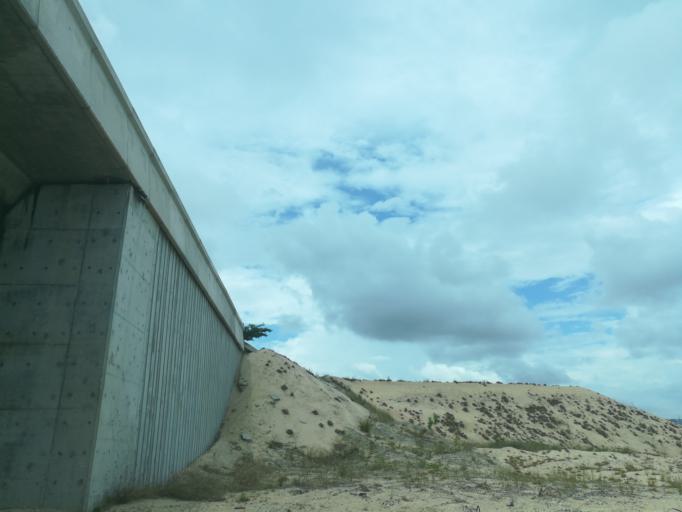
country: NG
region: Lagos
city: Ikoyi
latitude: 6.4143
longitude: 3.4184
